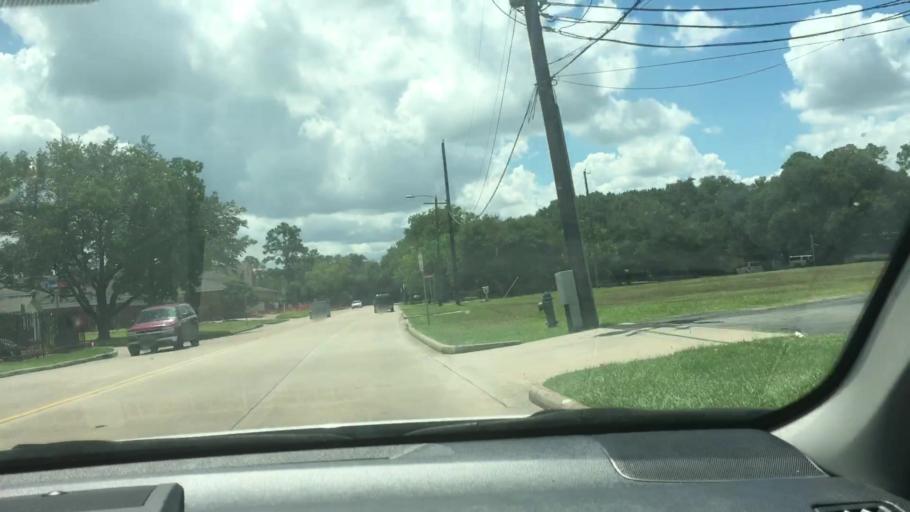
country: US
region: Texas
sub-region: Fort Bend County
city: Missouri City
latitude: 29.6148
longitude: -95.5467
